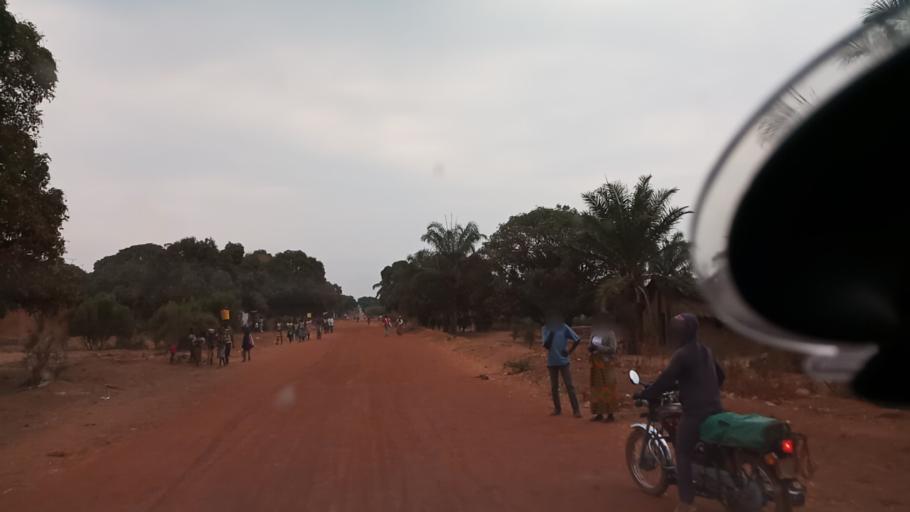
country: ZM
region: Luapula
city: Nchelenge
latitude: -9.2768
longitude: 28.3304
